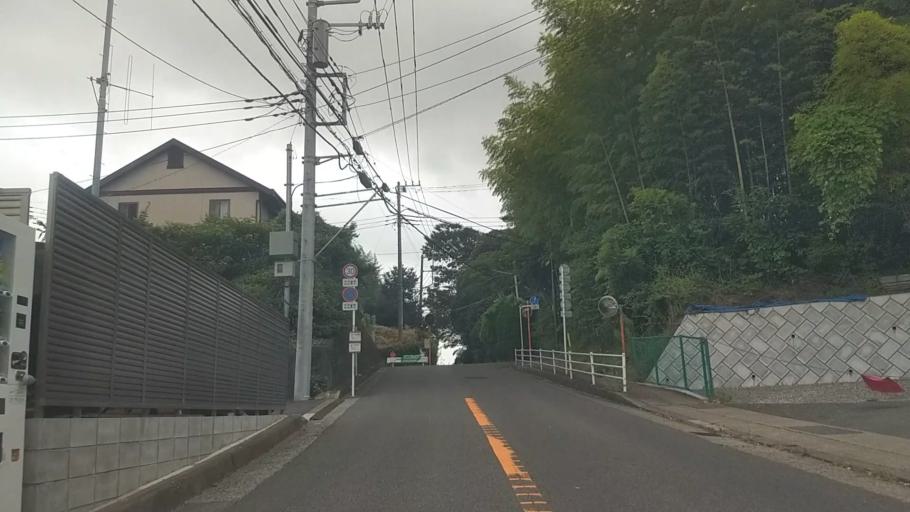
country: JP
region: Kanagawa
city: Yokosuka
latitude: 35.2312
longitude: 139.6497
